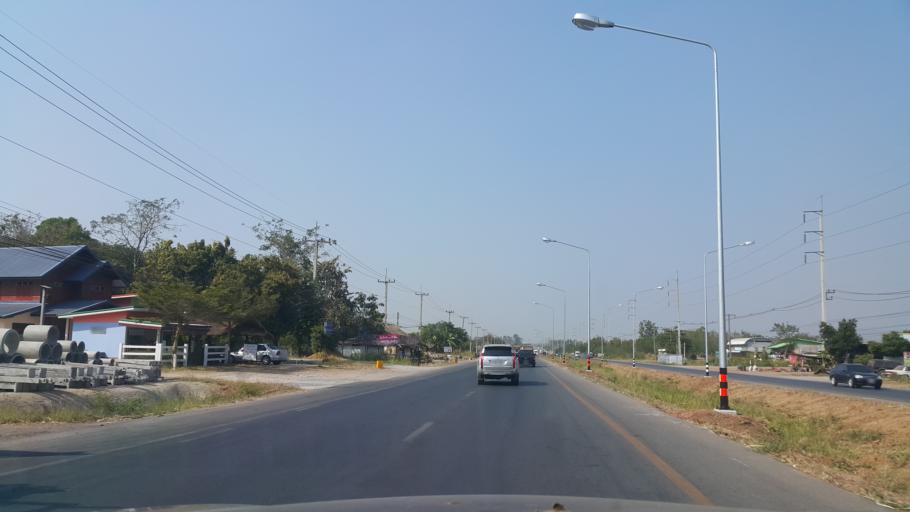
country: TH
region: Chaiyaphum
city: Phu Khiao
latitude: 16.4266
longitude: 102.1296
